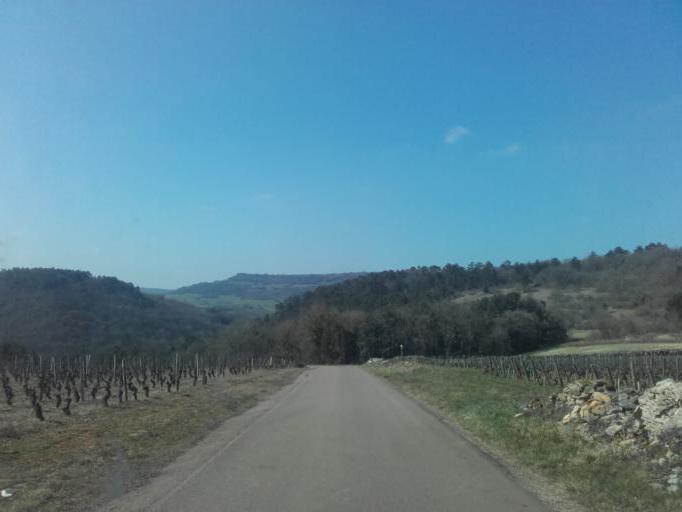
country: FR
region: Bourgogne
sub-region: Departement de la Cote-d'Or
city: Savigny-les-Beaune
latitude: 47.0527
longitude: 4.7612
